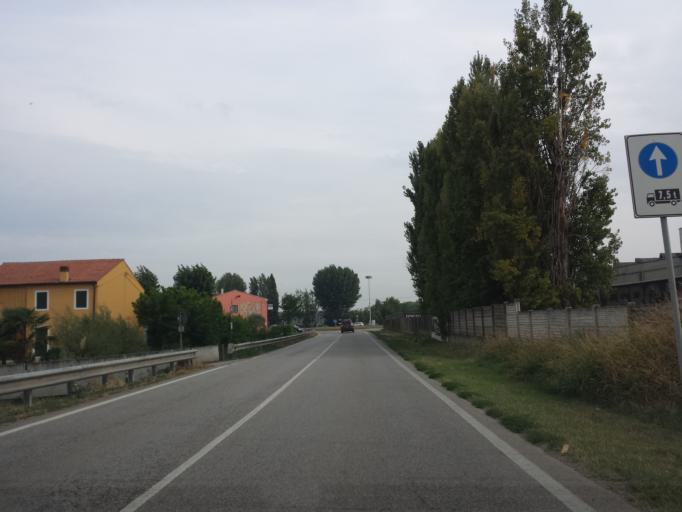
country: IT
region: Veneto
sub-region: Provincia di Verona
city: San Gregorio
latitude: 45.3453
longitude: 11.2908
